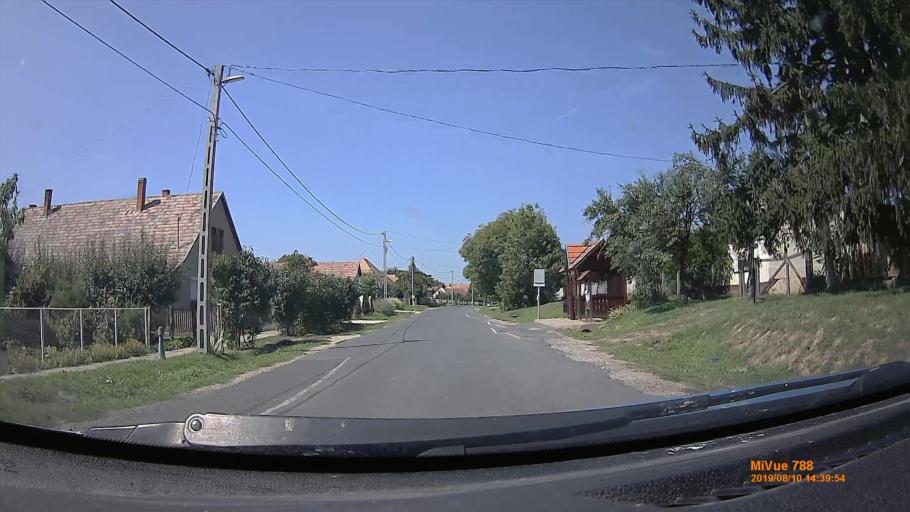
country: HU
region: Somogy
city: Somogyvar
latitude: 46.5715
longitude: 17.6792
